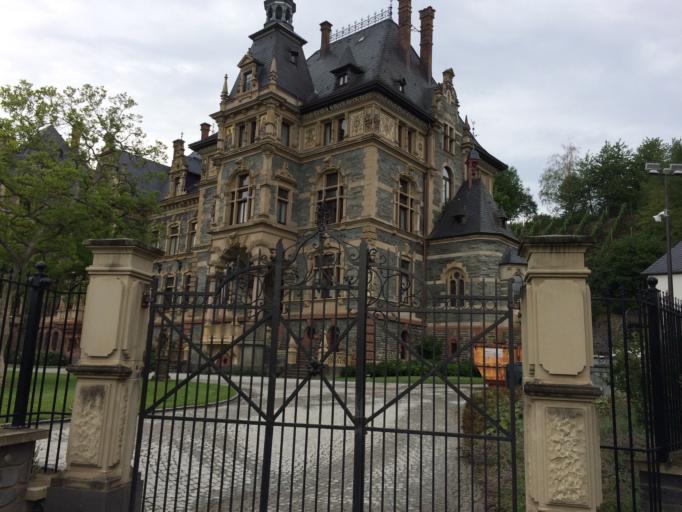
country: DE
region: Rheinland-Pfalz
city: Lieser
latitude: 49.9171
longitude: 7.0201
